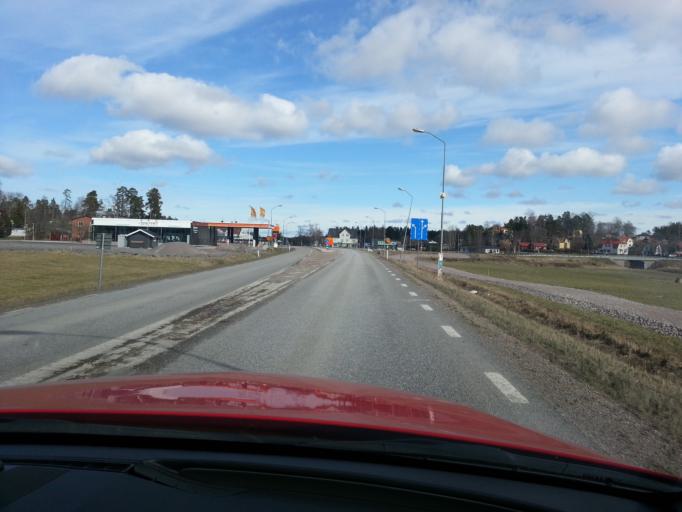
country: SE
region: Uppsala
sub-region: Osthammars Kommun
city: Gimo
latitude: 60.0613
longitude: 18.0768
